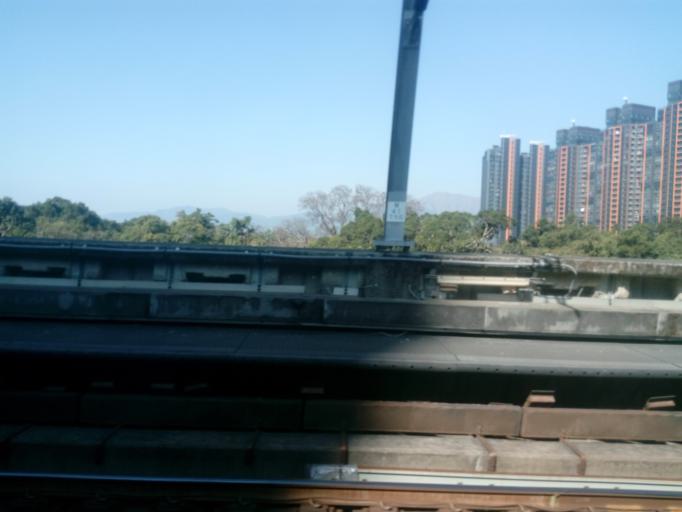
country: HK
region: Sai Kung
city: Sai Kung
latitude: 22.4283
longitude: 114.2416
